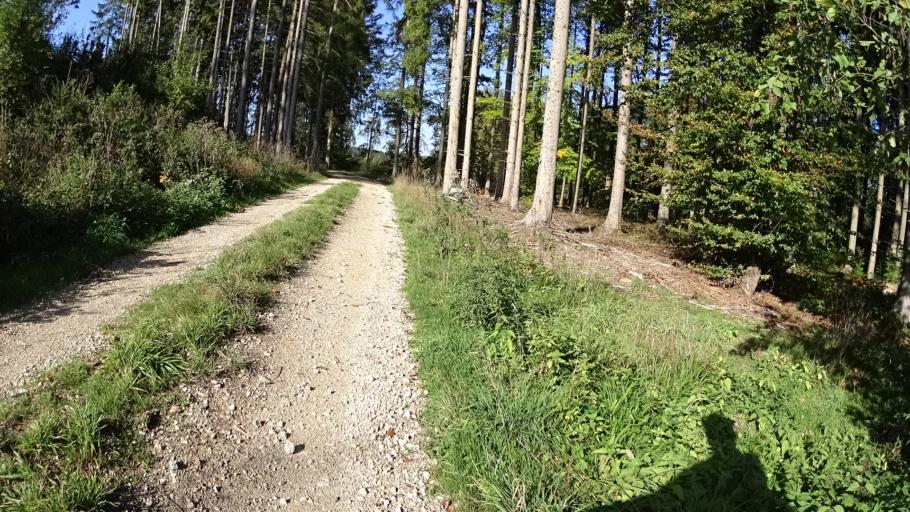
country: DE
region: Bavaria
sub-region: Upper Bavaria
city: Bohmfeld
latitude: 48.8844
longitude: 11.3604
